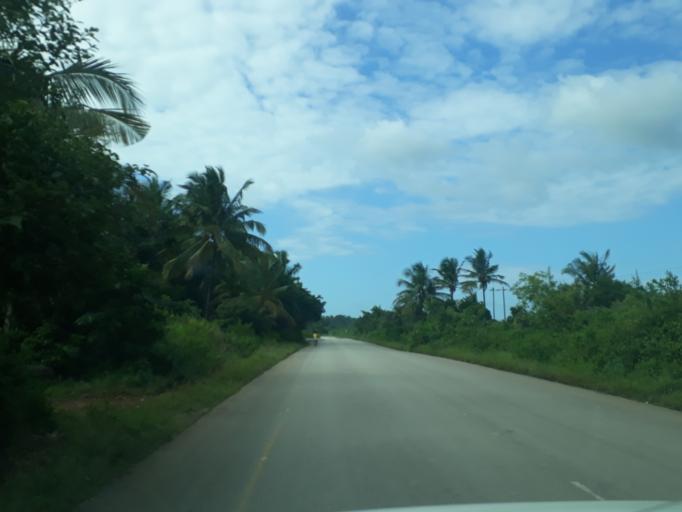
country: TZ
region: Zanzibar North
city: Kijini
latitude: -5.8390
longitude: 39.2859
